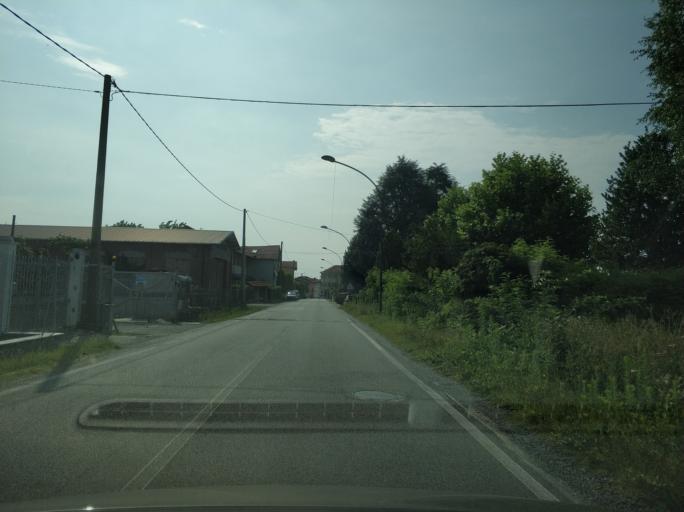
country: IT
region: Piedmont
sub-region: Provincia di Torino
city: Mathi
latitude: 45.2604
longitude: 7.5372
